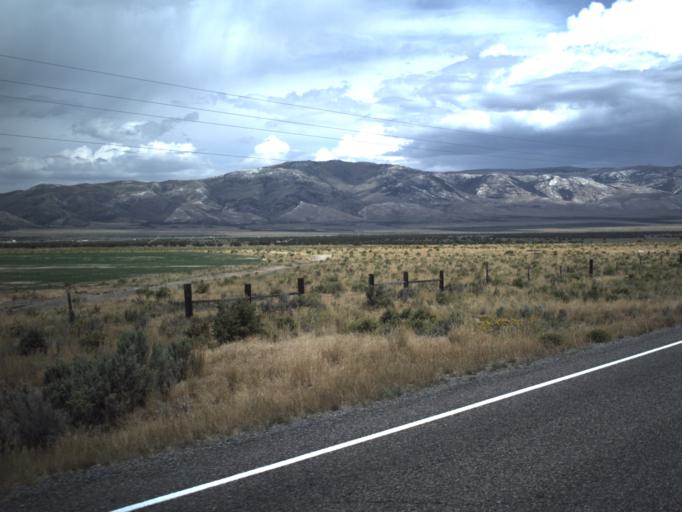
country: US
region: Idaho
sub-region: Cassia County
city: Burley
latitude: 41.7659
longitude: -113.5083
